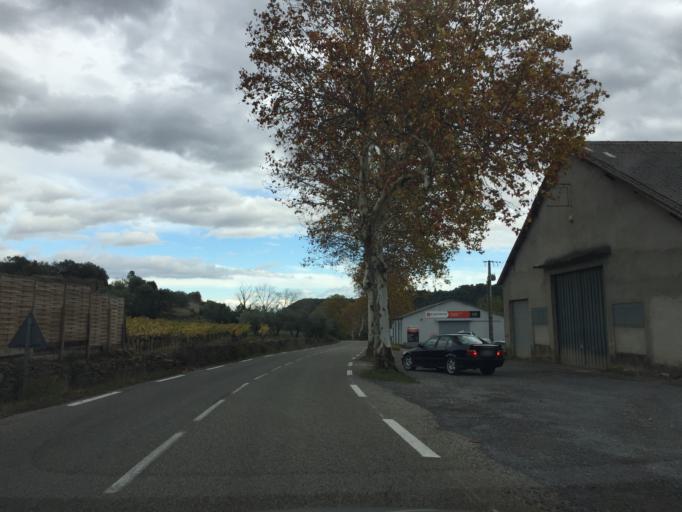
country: FR
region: Rhone-Alpes
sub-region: Departement de l'Ardeche
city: Les Vans
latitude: 44.4085
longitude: 4.1123
